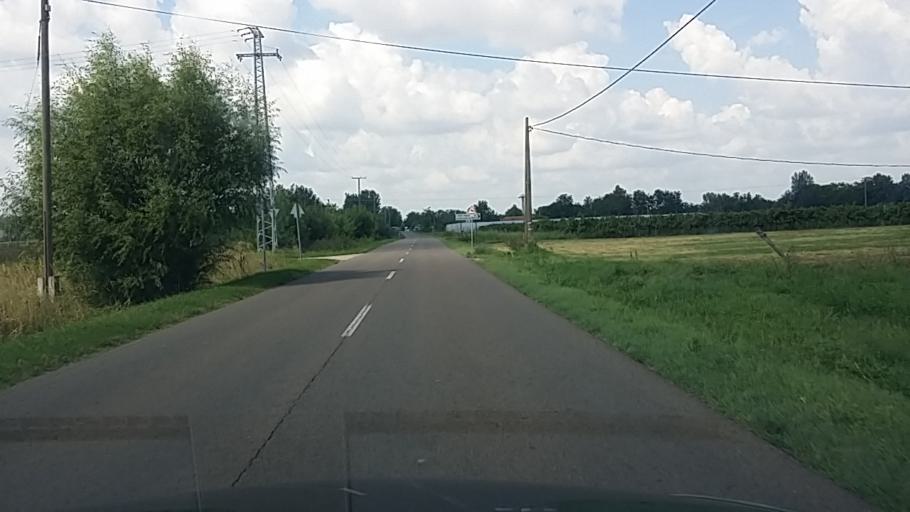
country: HU
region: Bacs-Kiskun
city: Tiszaalpar
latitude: 46.7428
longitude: 20.0510
